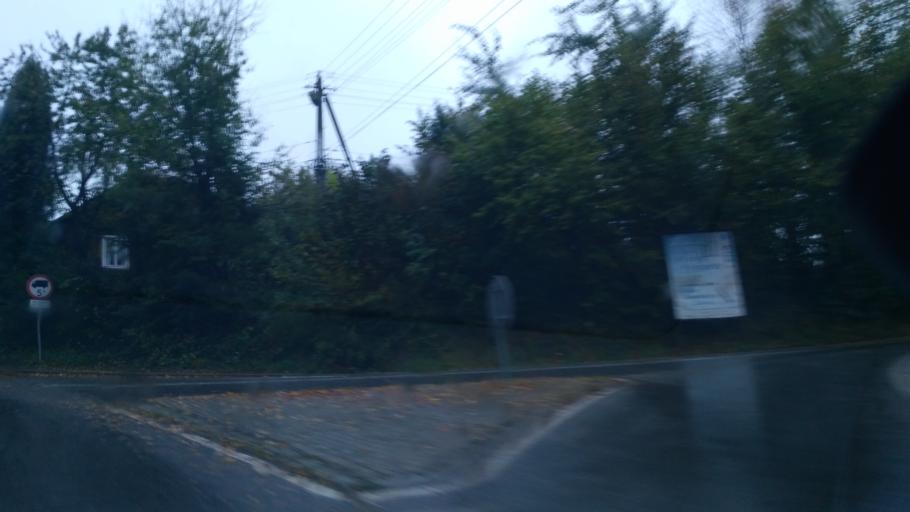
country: PL
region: Subcarpathian Voivodeship
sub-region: Powiat krosnienski
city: Kroscienko Wyzne
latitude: 49.6825
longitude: 21.8122
